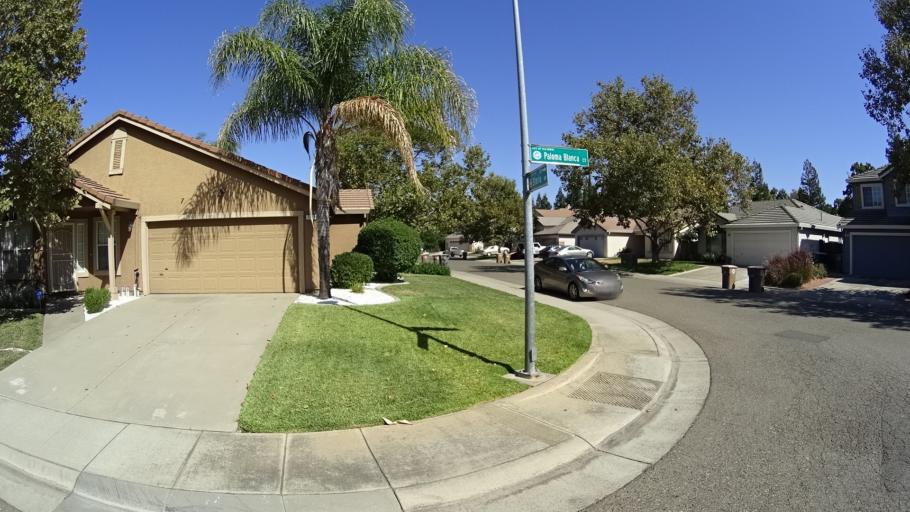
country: US
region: California
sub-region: Sacramento County
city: Laguna
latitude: 38.4267
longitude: -121.4218
